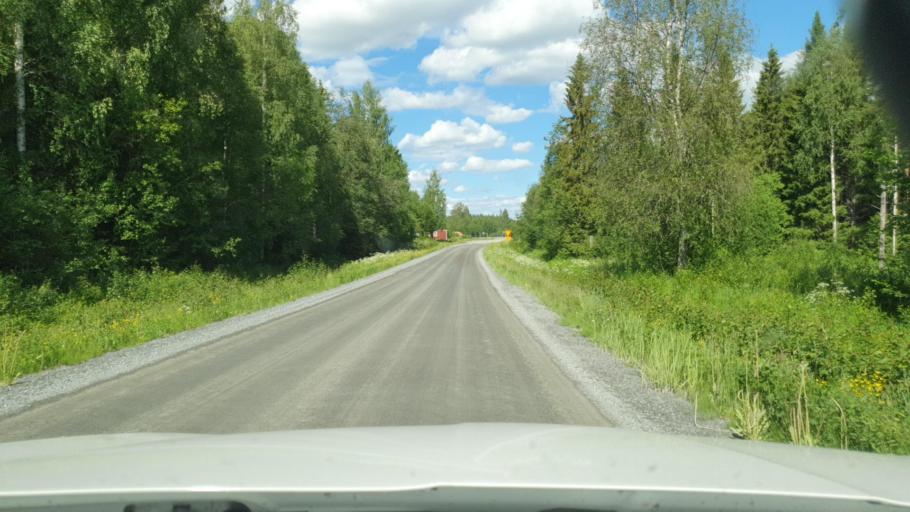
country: SE
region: Vaesterbotten
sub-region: Skelleftea Kommun
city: Forsbacka
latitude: 64.8395
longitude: 20.5053
